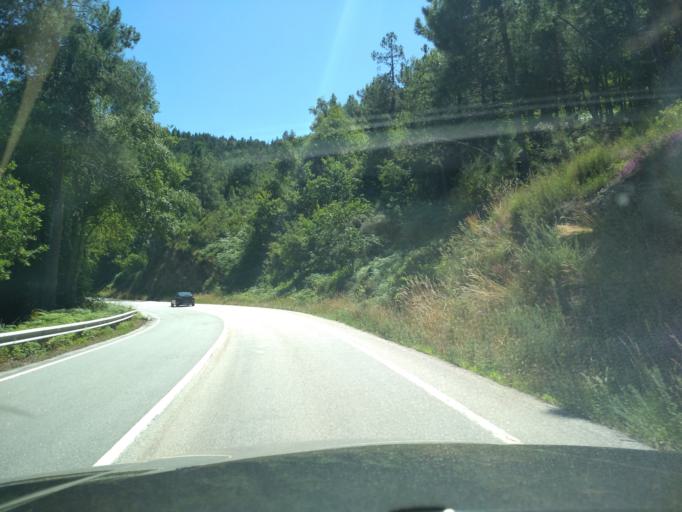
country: PT
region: Vila Real
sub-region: Ribeira de Pena
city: Ribeira de Pena
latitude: 41.5126
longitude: -7.7977
